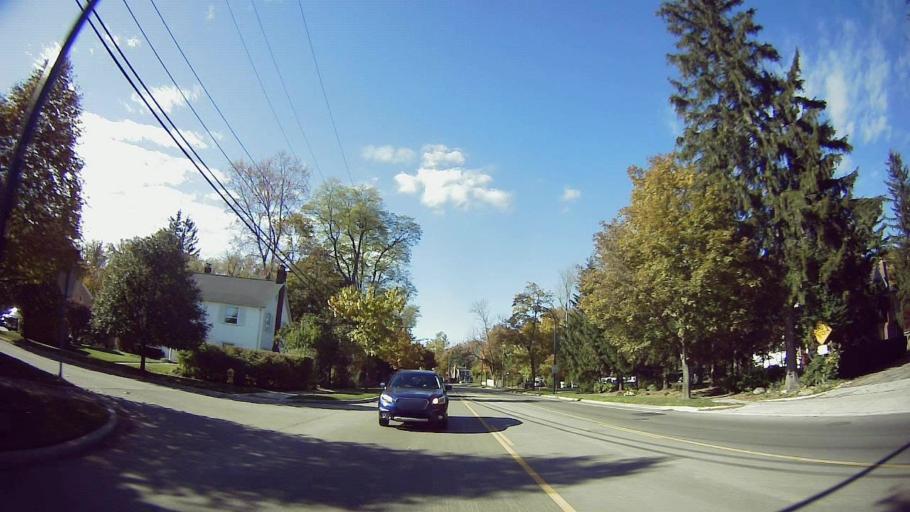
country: US
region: Michigan
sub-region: Oakland County
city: Birmingham
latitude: 42.5457
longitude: -83.2251
